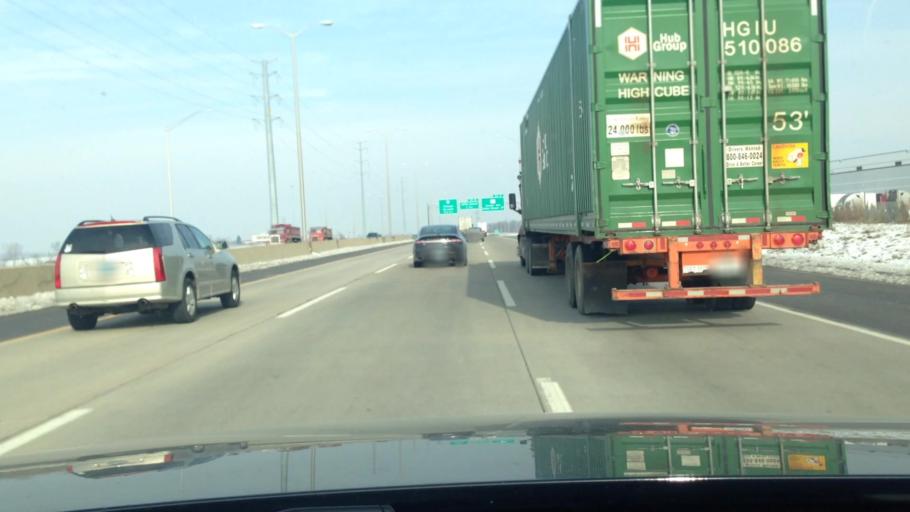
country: US
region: Illinois
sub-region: Will County
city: Lockport
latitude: 41.6197
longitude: -88.0122
